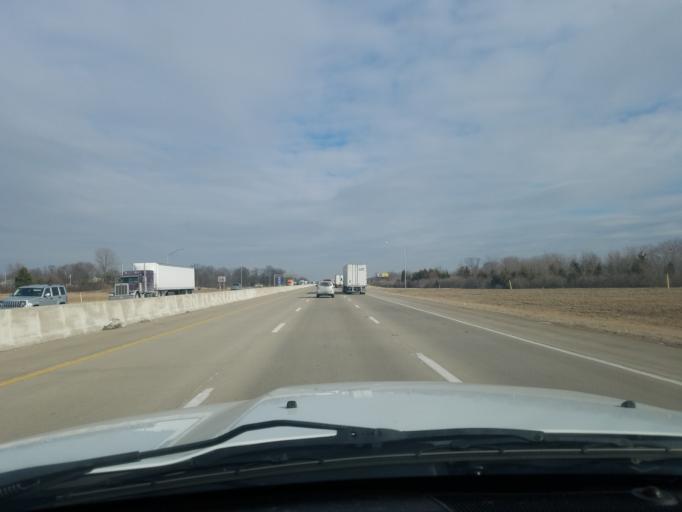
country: US
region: Indiana
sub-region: Marion County
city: Lawrence
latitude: 39.8007
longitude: -86.0072
